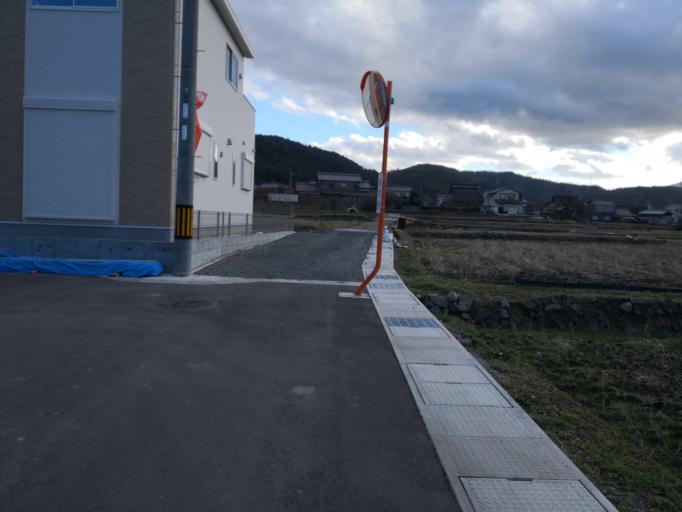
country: JP
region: Kyoto
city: Kameoka
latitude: 34.9921
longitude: 135.5483
